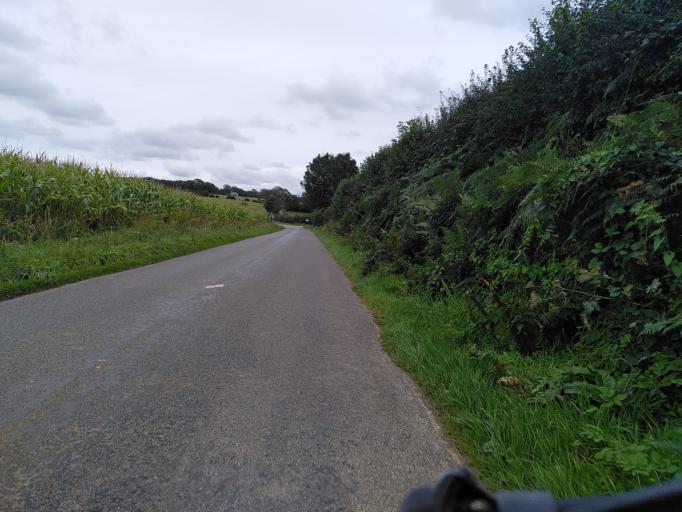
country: FR
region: Nord-Pas-de-Calais
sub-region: Departement du Pas-de-Calais
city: Desvres
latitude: 50.6624
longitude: 1.8859
